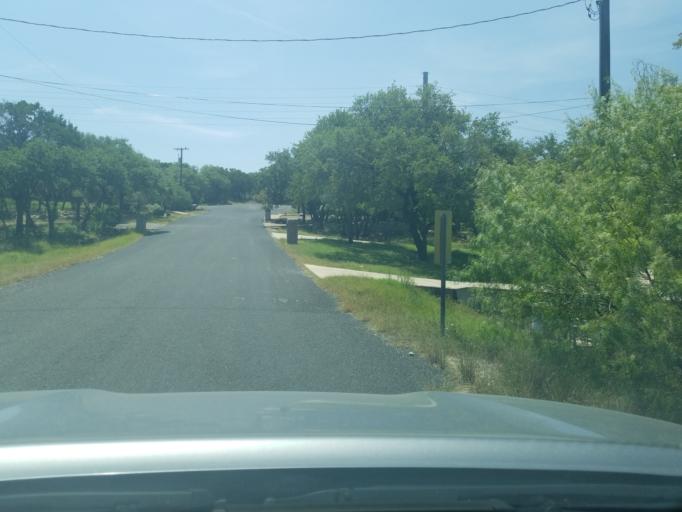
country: US
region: Texas
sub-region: Bexar County
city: Timberwood Park
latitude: 29.6671
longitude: -98.5162
